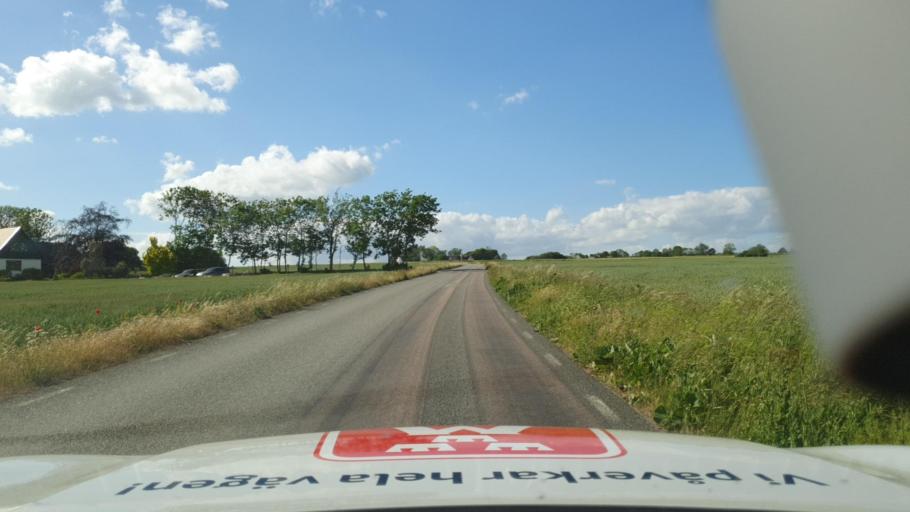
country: SE
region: Skane
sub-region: Simrishamns Kommun
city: Simrishamn
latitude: 55.5613
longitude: 14.3083
